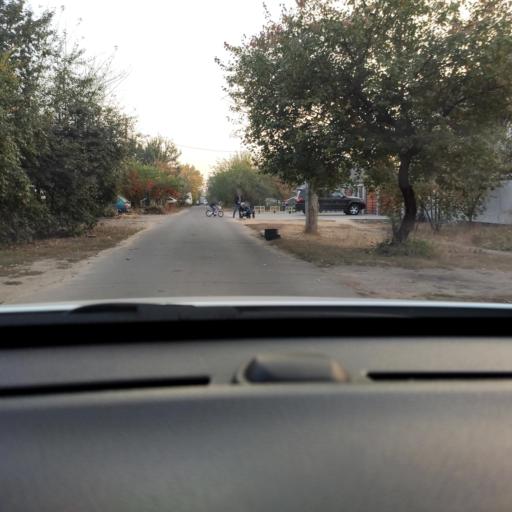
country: RU
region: Voronezj
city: Voronezh
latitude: 51.6645
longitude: 39.2608
